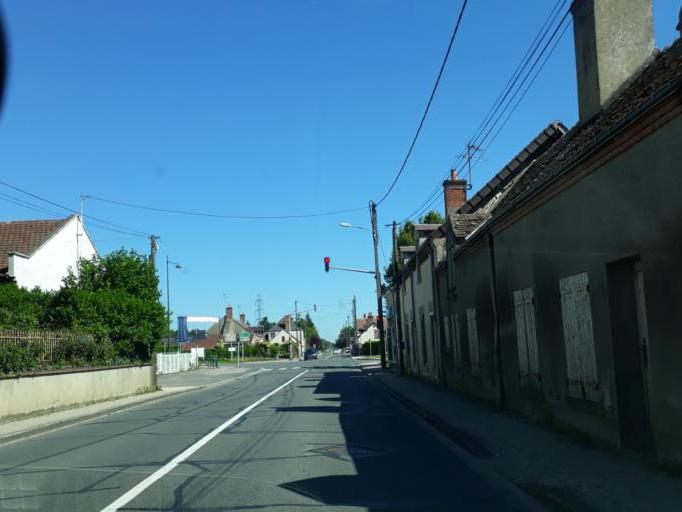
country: FR
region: Centre
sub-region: Departement du Loiret
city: Bray-en-Val
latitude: 47.8143
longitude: 2.4008
